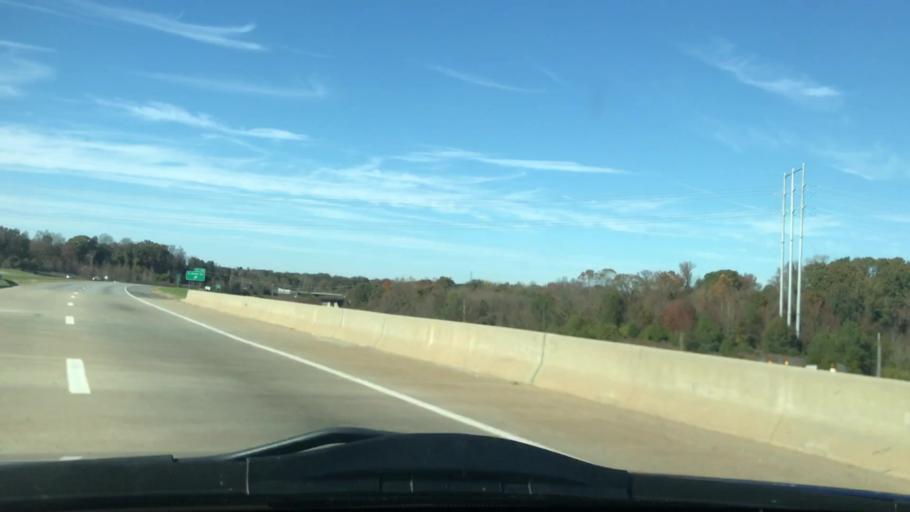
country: US
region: North Carolina
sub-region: Randolph County
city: Archdale
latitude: 35.9461
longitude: -79.9729
